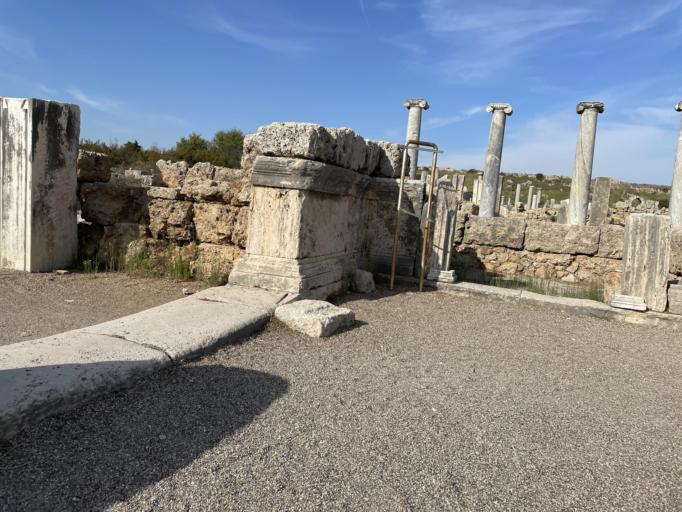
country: TR
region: Antalya
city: Aksu
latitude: 36.9617
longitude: 30.8545
